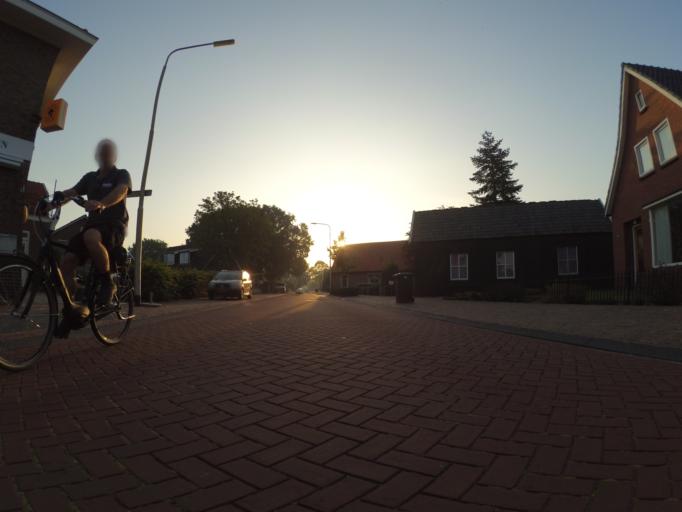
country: NL
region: Overijssel
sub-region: Gemeente Twenterand
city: Vriezenveen
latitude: 52.4163
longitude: 6.6376
